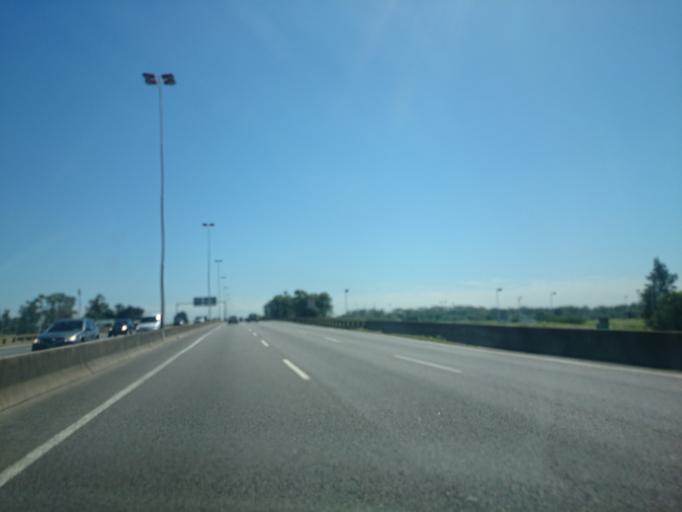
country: AR
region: Buenos Aires F.D.
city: Villa Lugano
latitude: -34.7285
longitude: -58.5161
